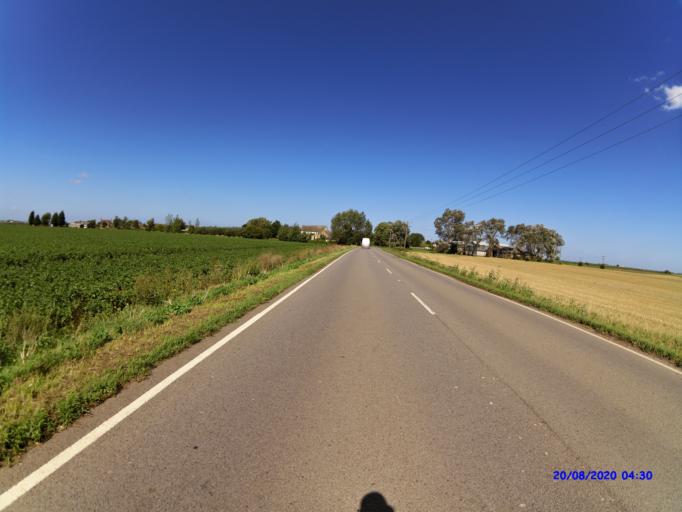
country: GB
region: England
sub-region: Cambridgeshire
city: Whittlesey
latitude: 52.5088
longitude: -0.1398
